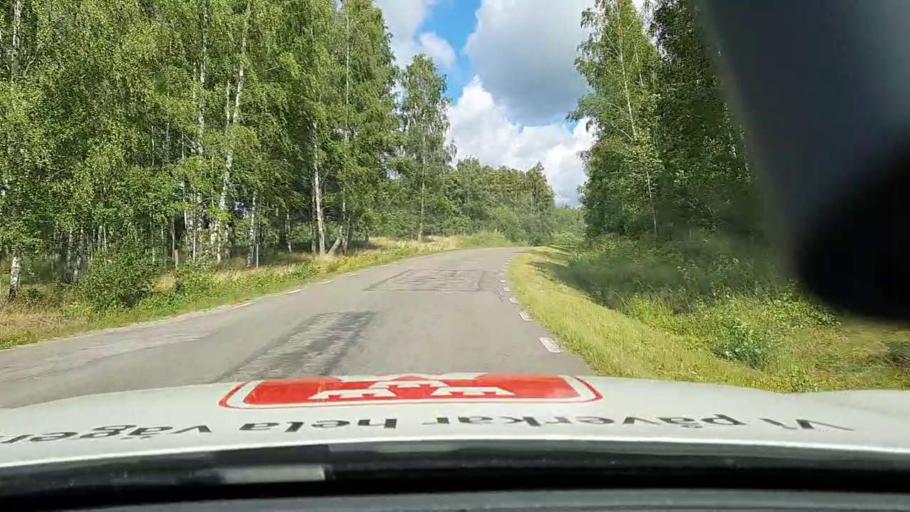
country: SE
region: Vaestra Goetaland
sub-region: Karlsborgs Kommun
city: Molltorp
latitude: 58.5985
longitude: 14.2647
